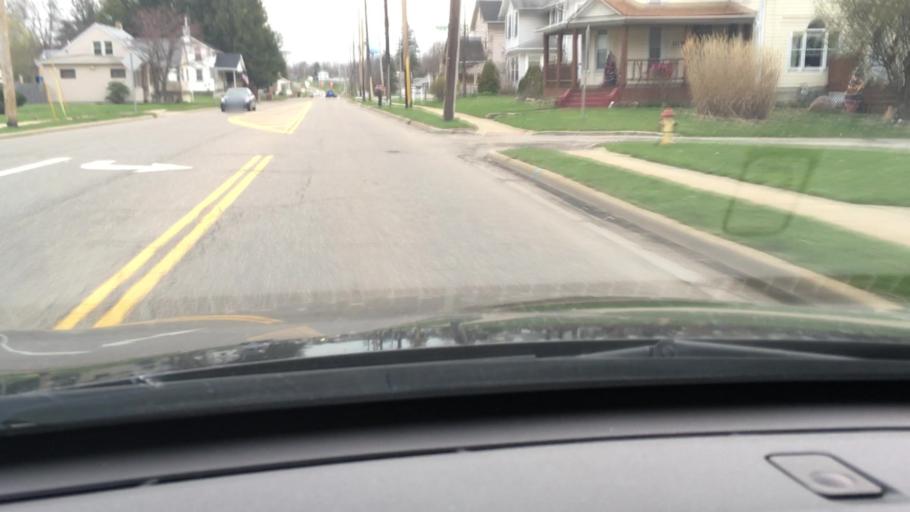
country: US
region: Ohio
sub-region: Columbiana County
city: Columbiana
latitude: 40.9475
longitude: -80.6594
